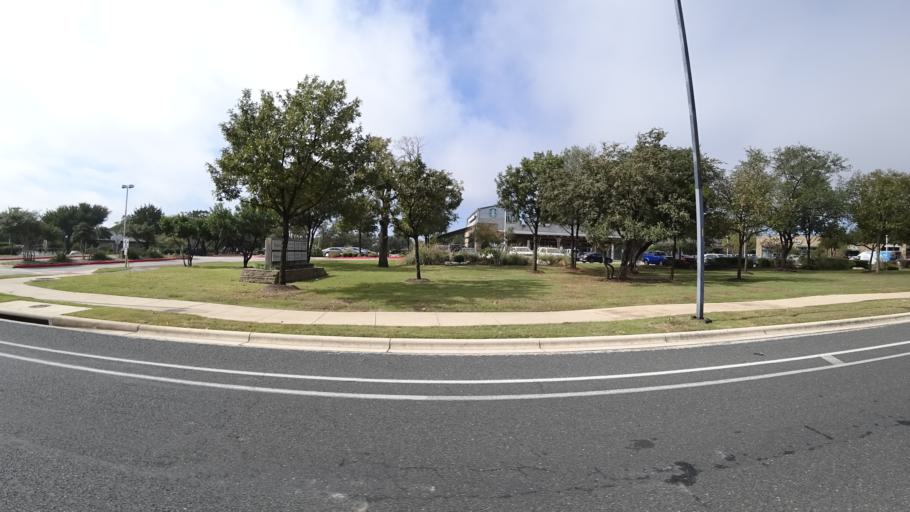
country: US
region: Texas
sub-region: Travis County
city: Shady Hollow
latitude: 30.2028
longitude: -97.8781
